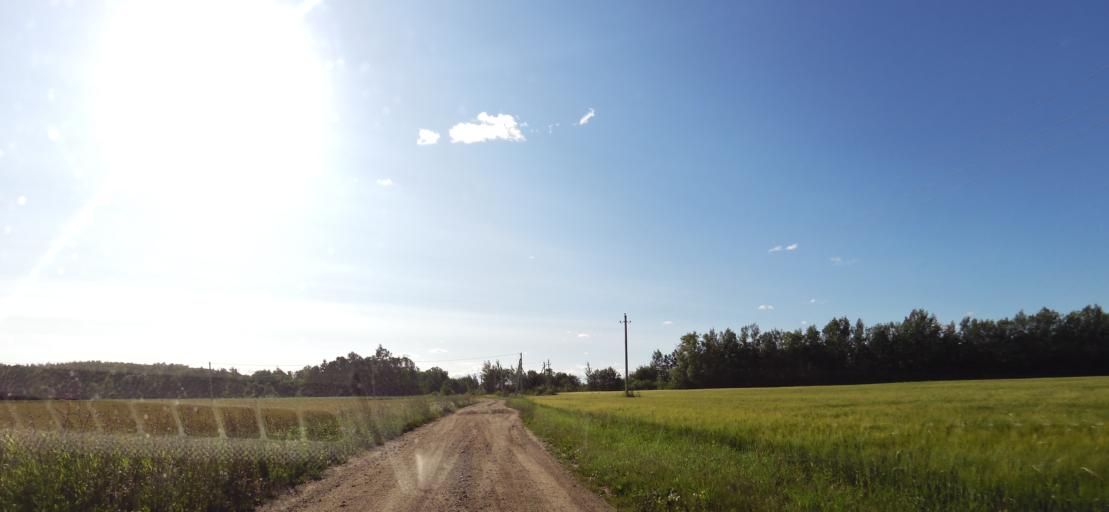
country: LT
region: Panevezys
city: Pasvalys
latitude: 56.1283
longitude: 24.5602
